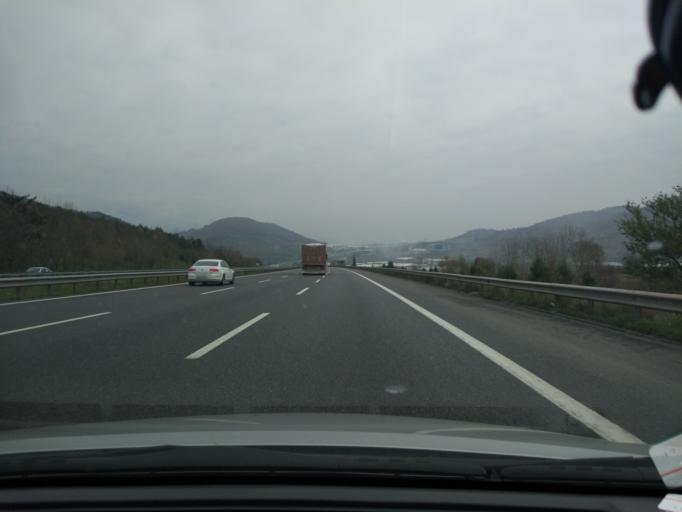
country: TR
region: Duzce
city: Gumusova
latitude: 40.8309
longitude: 30.9340
